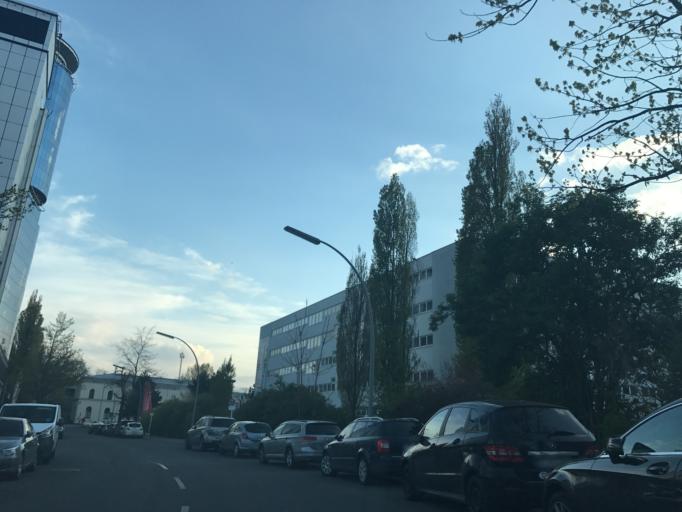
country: DE
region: Berlin
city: Spandau
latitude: 52.5335
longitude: 13.2102
